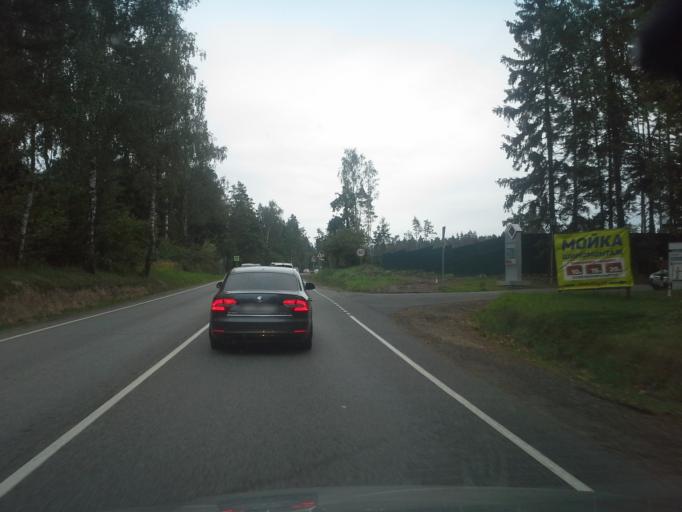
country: RU
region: Moskovskaya
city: Zhavoronki
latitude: 55.7059
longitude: 37.0975
